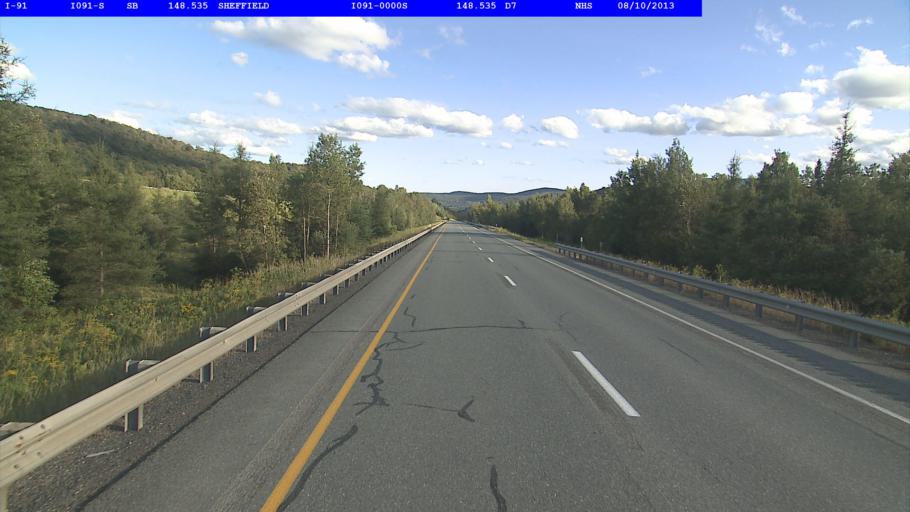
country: US
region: Vermont
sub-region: Caledonia County
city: Lyndonville
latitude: 44.6435
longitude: -72.1324
